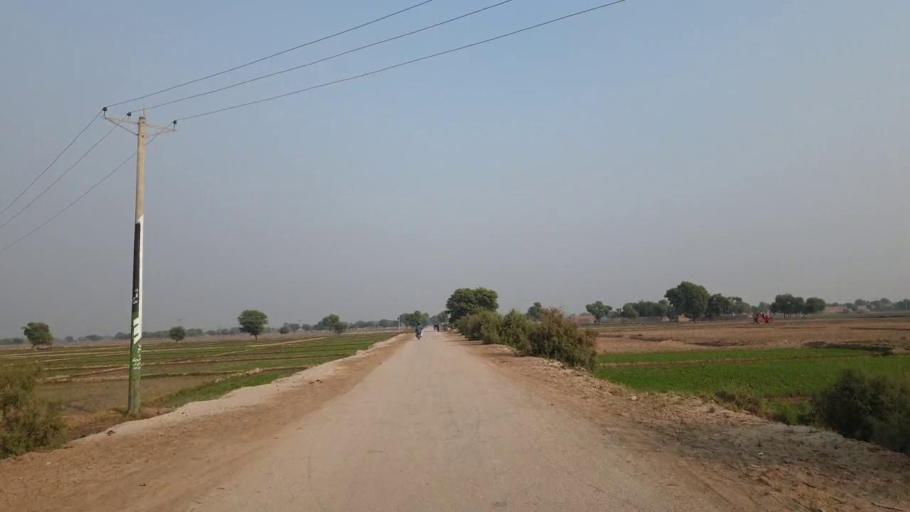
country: PK
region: Sindh
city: Bhan
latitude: 26.4960
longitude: 67.7320
